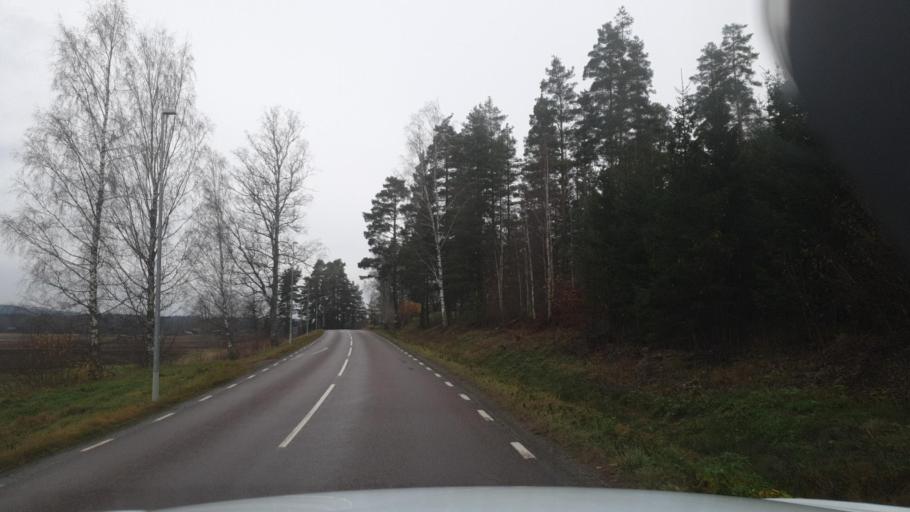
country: SE
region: Vaermland
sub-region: Arvika Kommun
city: Arvika
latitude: 59.5632
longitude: 12.5567
